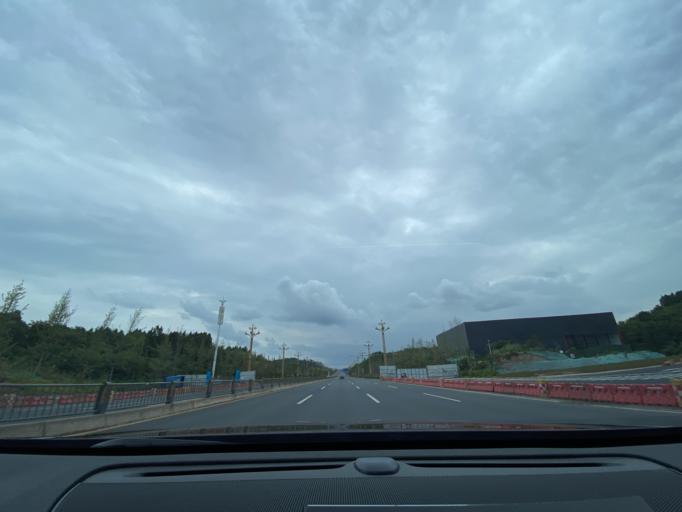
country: CN
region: Sichuan
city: Jiancheng
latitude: 30.4607
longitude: 104.4957
